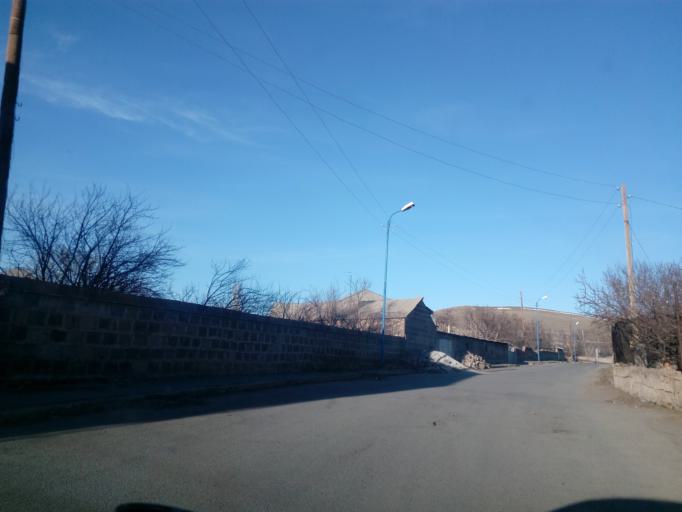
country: AM
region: Aragatsotn
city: T'alin
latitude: 40.4492
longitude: 43.8777
